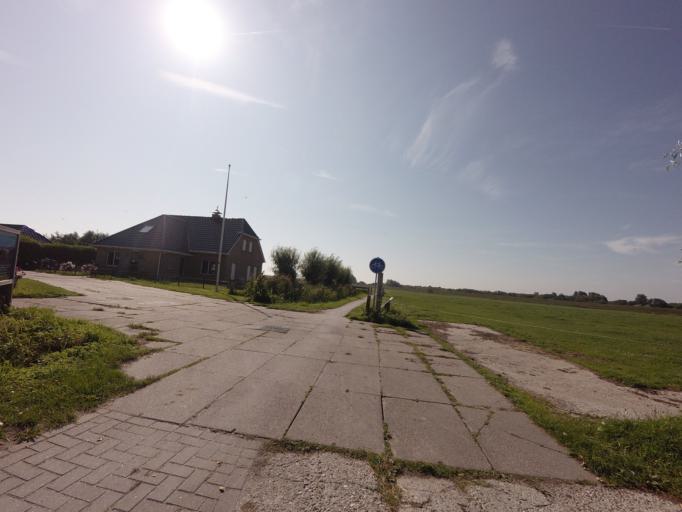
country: NL
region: Friesland
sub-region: Gemeente Schiermonnikoog
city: Schiermonnikoog
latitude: 53.4757
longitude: 6.1548
